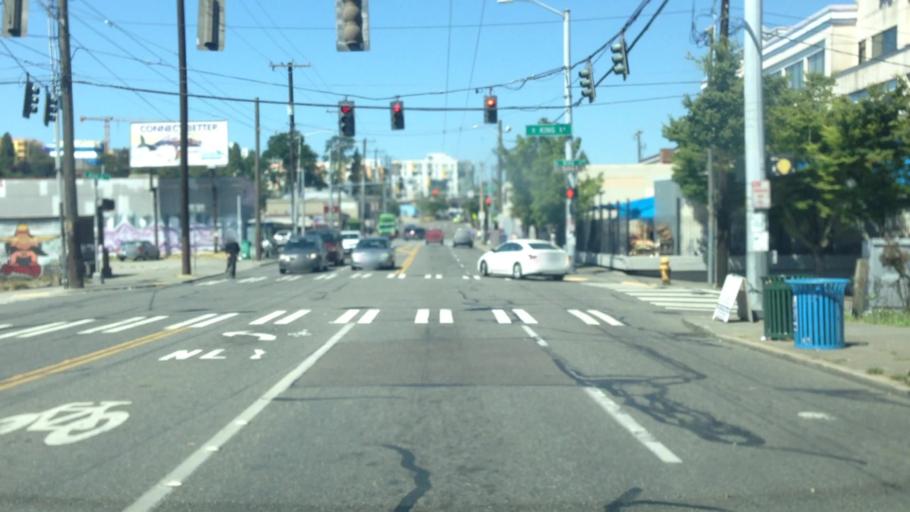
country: US
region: Washington
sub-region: King County
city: Seattle
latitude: 47.5981
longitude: -122.3172
